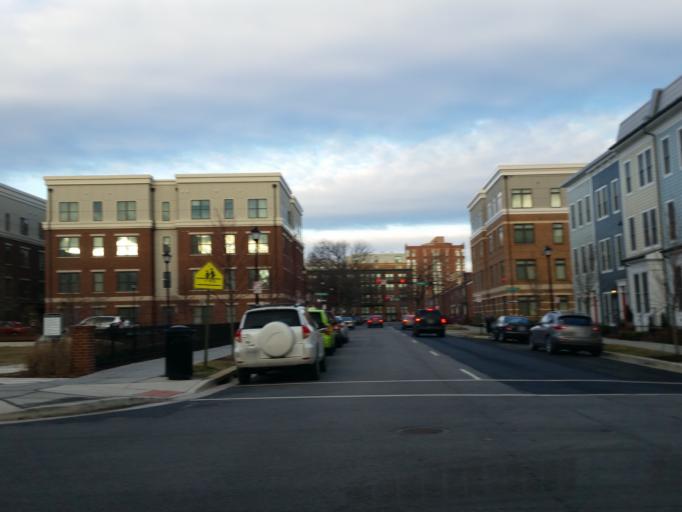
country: US
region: Virginia
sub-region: City of Alexandria
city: Alexandria
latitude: 38.8144
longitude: -77.0472
